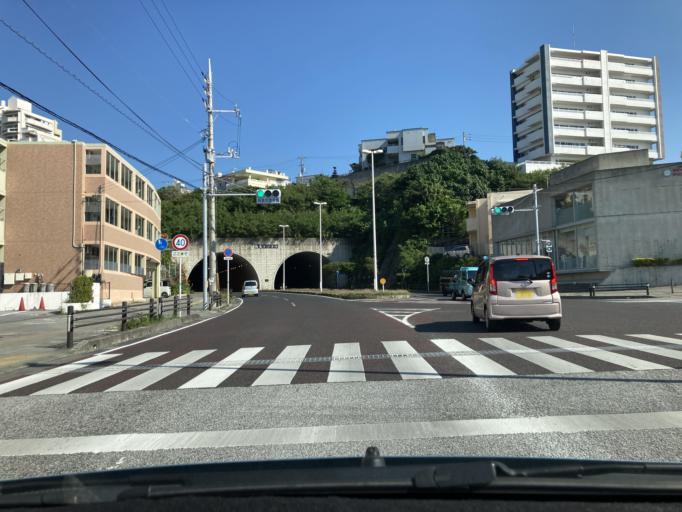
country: JP
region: Okinawa
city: Naha-shi
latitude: 26.2033
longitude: 127.7069
